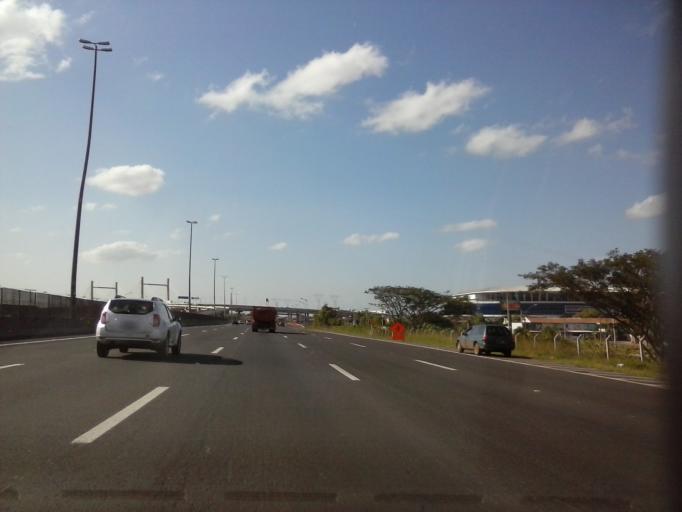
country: BR
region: Rio Grande do Sul
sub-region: Porto Alegre
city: Porto Alegre
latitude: -29.9801
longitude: -51.2008
